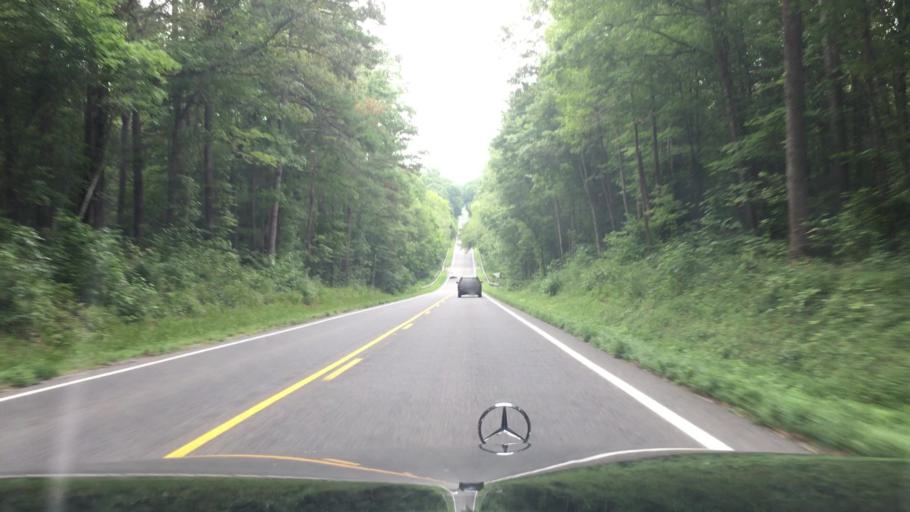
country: US
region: Virginia
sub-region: Nottoway County
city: Crewe
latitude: 37.2762
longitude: -78.1779
